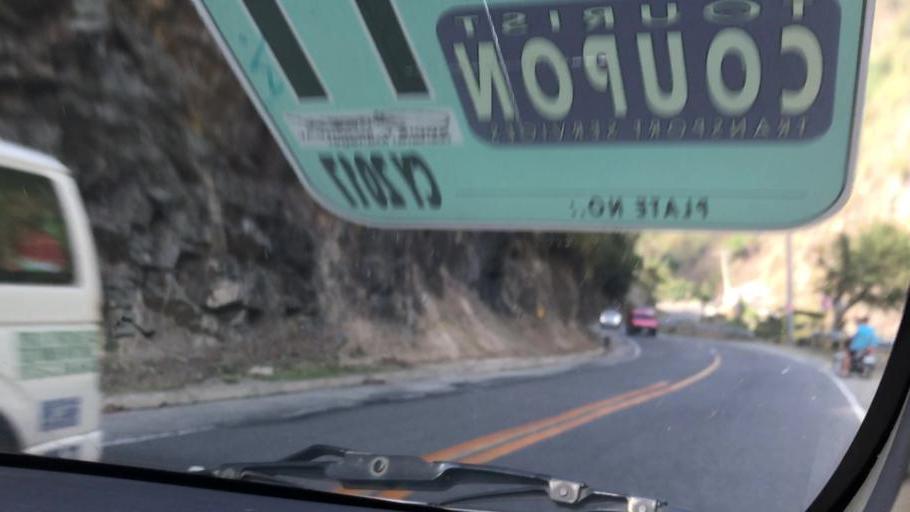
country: PH
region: Cordillera
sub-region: Province of Benguet
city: Tuba
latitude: 16.3209
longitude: 120.6149
